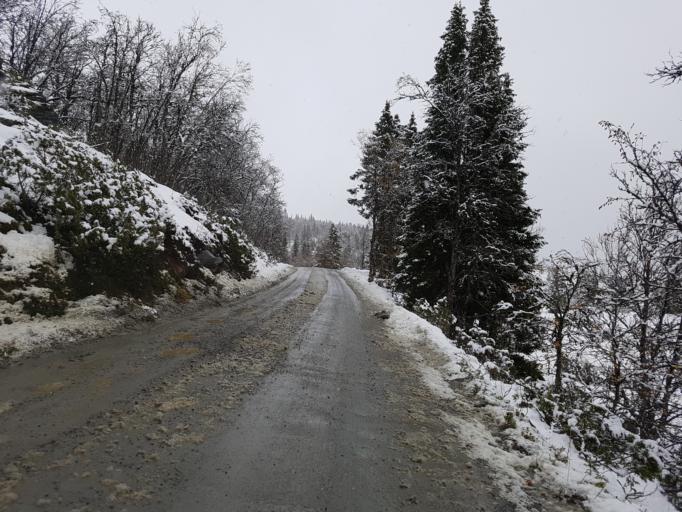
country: NO
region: Oppland
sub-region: Sel
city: Otta
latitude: 61.8021
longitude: 9.7041
